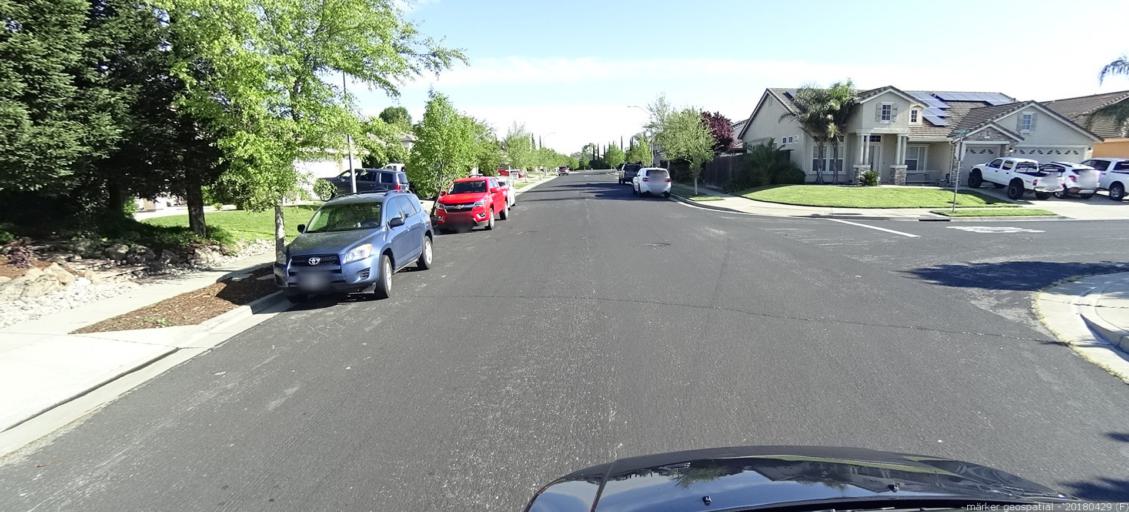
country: US
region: California
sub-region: Yolo County
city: West Sacramento
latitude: 38.5355
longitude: -121.5689
